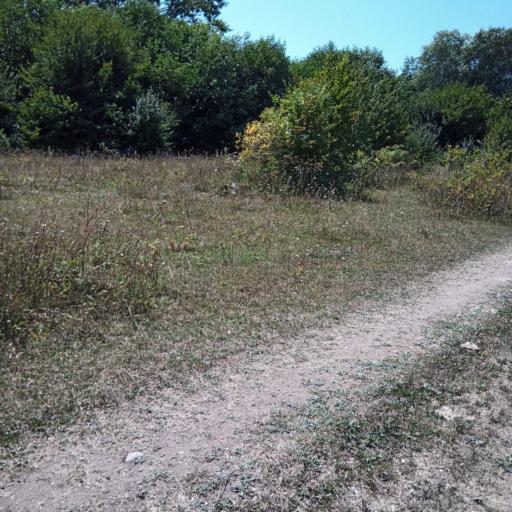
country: GE
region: Mtskheta-Mtianeti
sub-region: Tianetis Munitsip'alit'et'i
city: T'ianet'i
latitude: 42.0964
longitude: 44.9382
